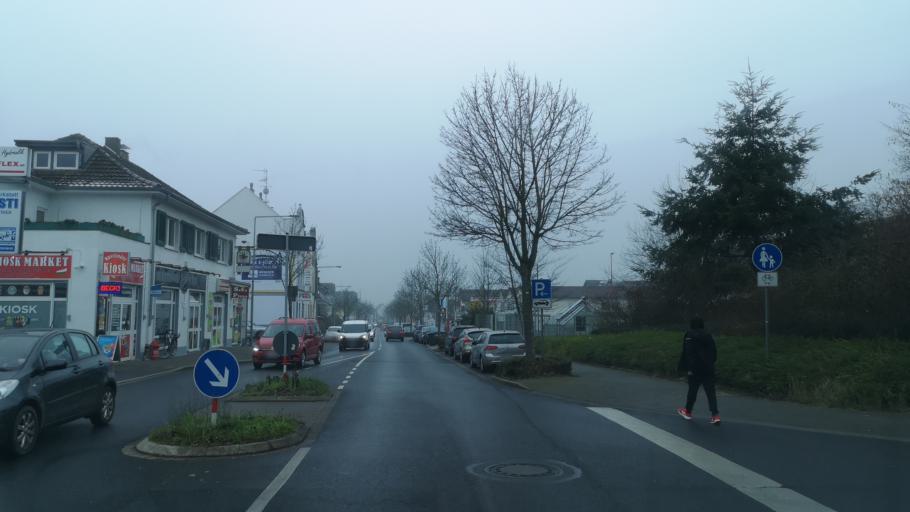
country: DE
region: North Rhine-Westphalia
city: Opladen
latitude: 51.0604
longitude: 7.0253
